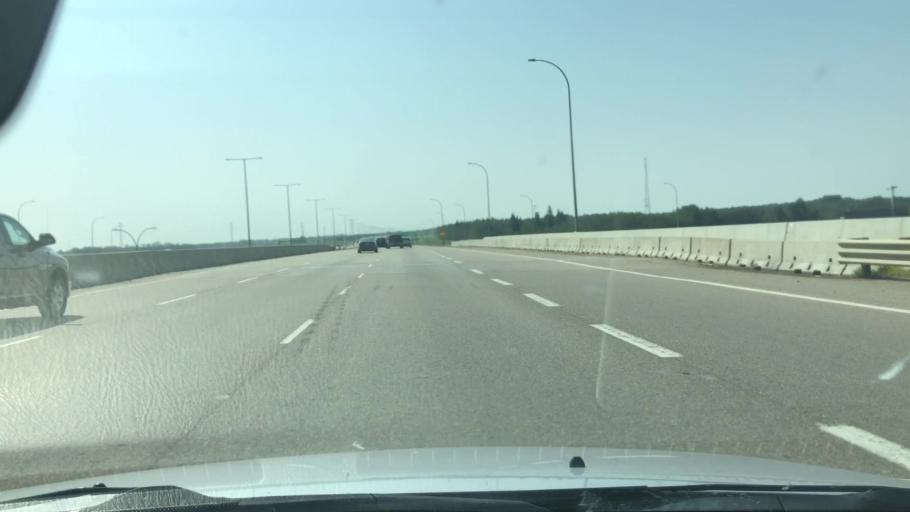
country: CA
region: Alberta
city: St. Albert
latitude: 53.5391
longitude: -113.6595
